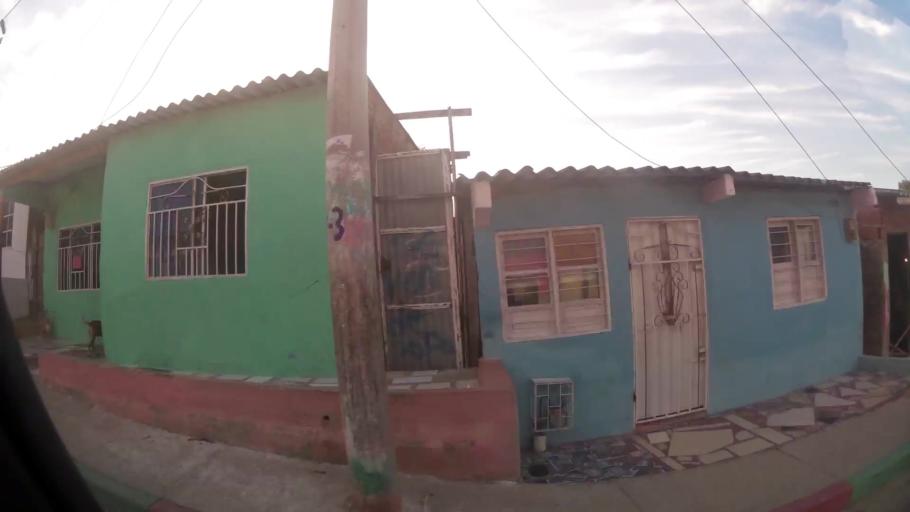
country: CO
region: Atlantico
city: Barranquilla
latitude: 10.9579
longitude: -74.8207
